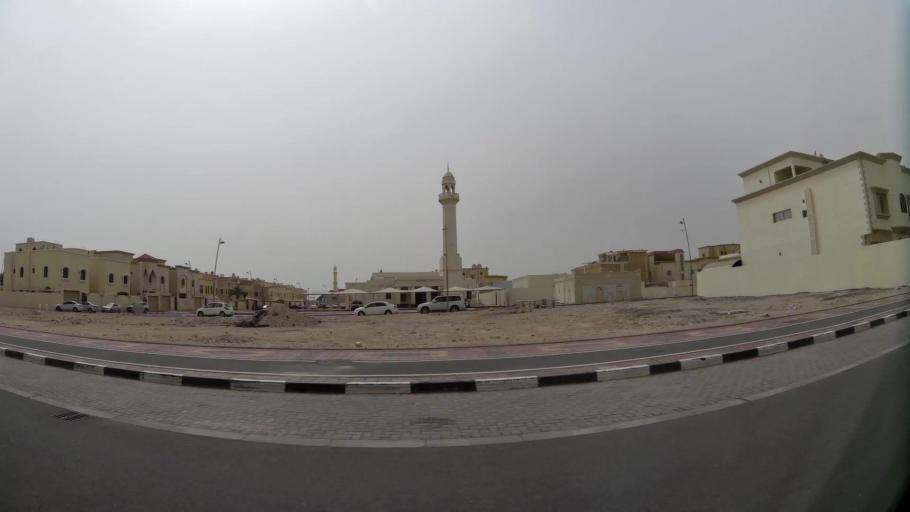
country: QA
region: Baladiyat ad Dawhah
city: Doha
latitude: 25.2311
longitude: 51.5393
